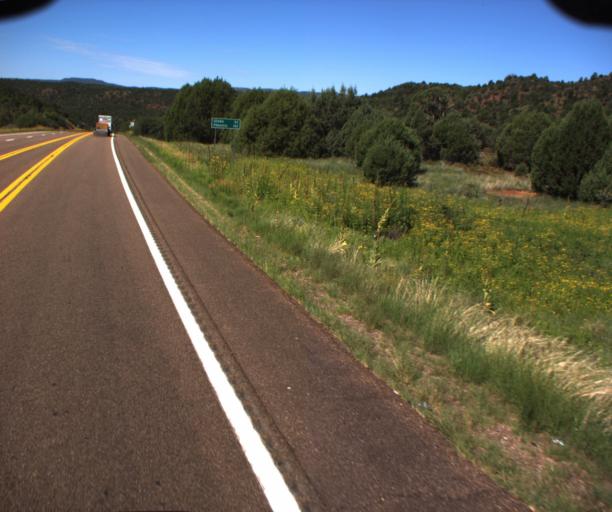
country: US
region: Arizona
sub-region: Navajo County
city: Cibecue
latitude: 34.0036
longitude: -110.2563
